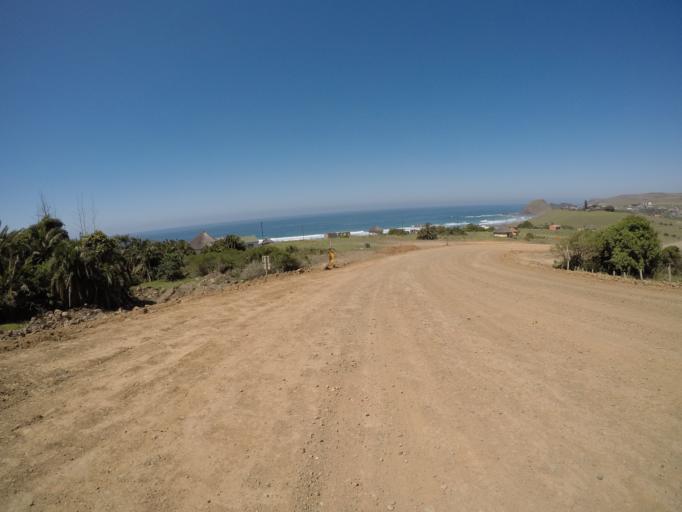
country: ZA
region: Eastern Cape
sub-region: OR Tambo District Municipality
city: Libode
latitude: -32.0265
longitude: 29.1163
